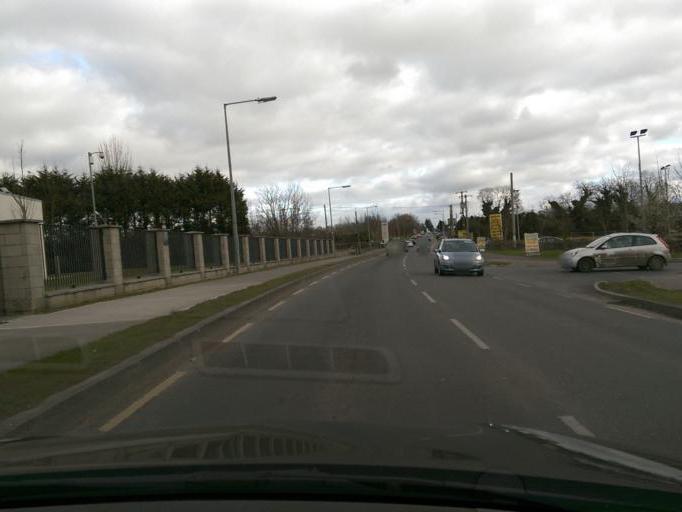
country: IE
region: Leinster
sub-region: An Iarmhi
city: Athlone
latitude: 53.4155
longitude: -7.8993
